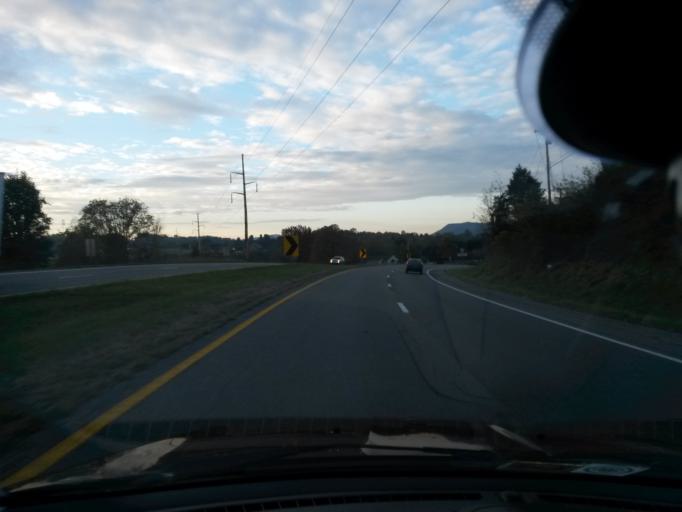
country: US
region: Virginia
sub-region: Botetourt County
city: Daleville
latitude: 37.4303
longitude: -79.9039
